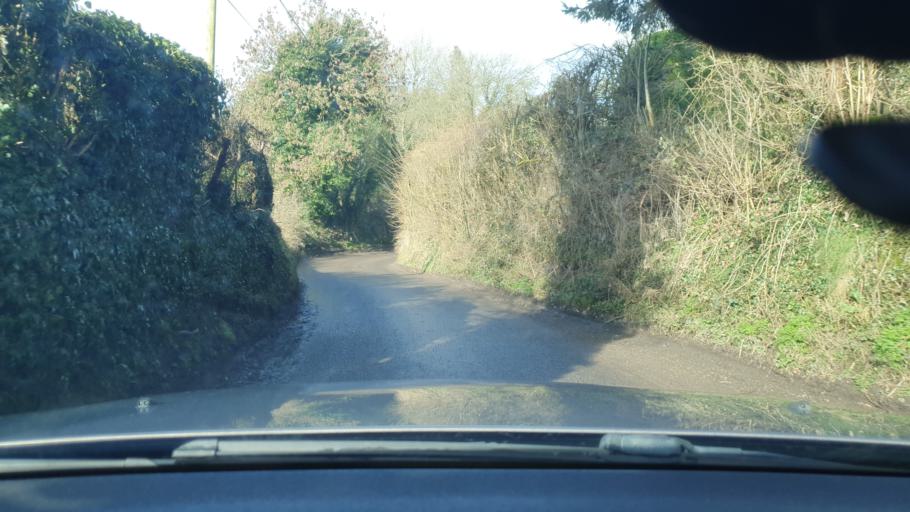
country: GB
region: England
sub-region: Wiltshire
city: Shalbourne
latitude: 51.3628
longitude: -1.5271
